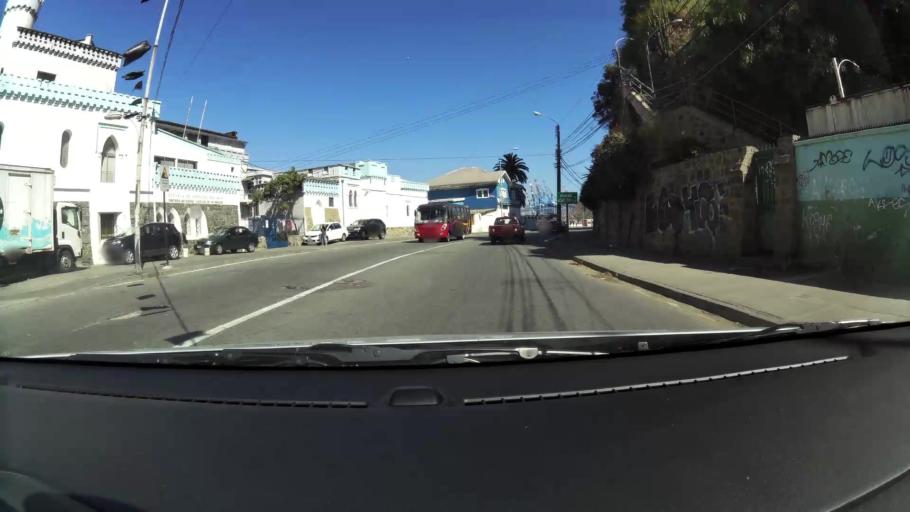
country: CL
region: Valparaiso
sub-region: Provincia de Valparaiso
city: Valparaiso
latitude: -33.0226
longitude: -71.6331
